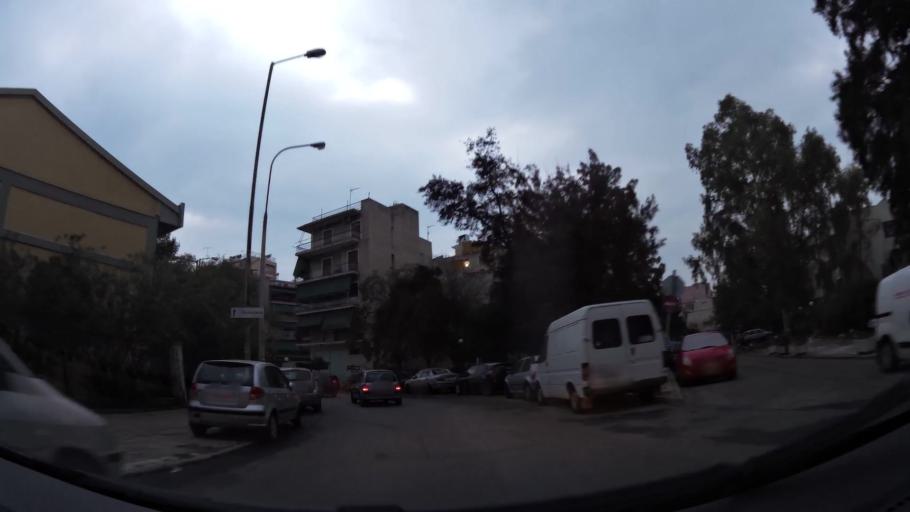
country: GR
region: Attica
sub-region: Nomarchia Athinas
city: Dhafni
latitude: 37.9523
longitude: 23.7394
